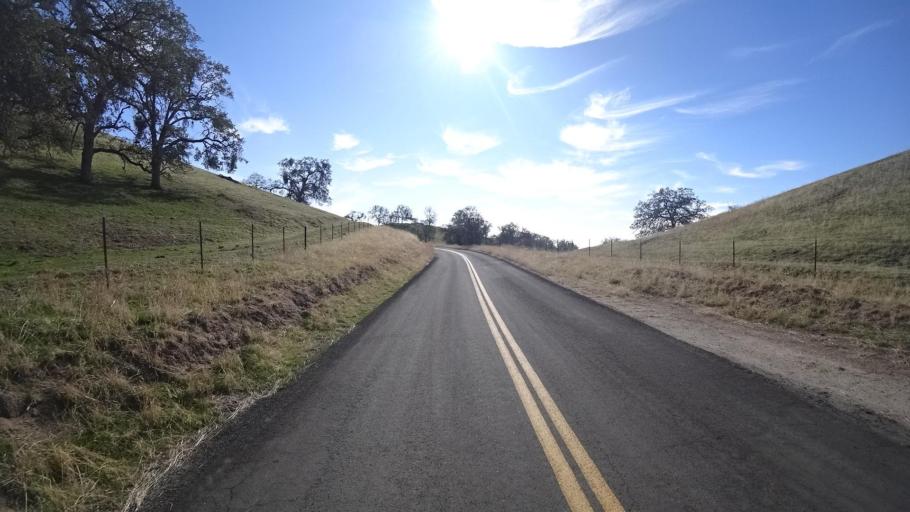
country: US
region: California
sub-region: Tulare County
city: Richgrove
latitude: 35.6604
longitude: -118.8437
